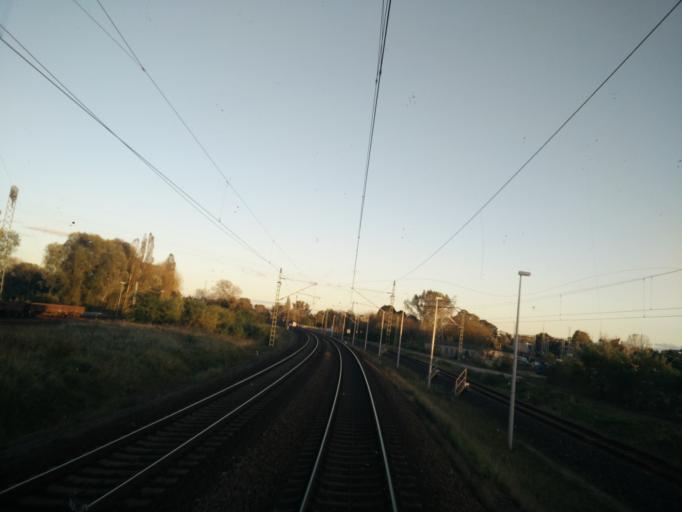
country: DE
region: Brandenburg
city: Wittenberge
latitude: 52.9948
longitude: 11.7702
